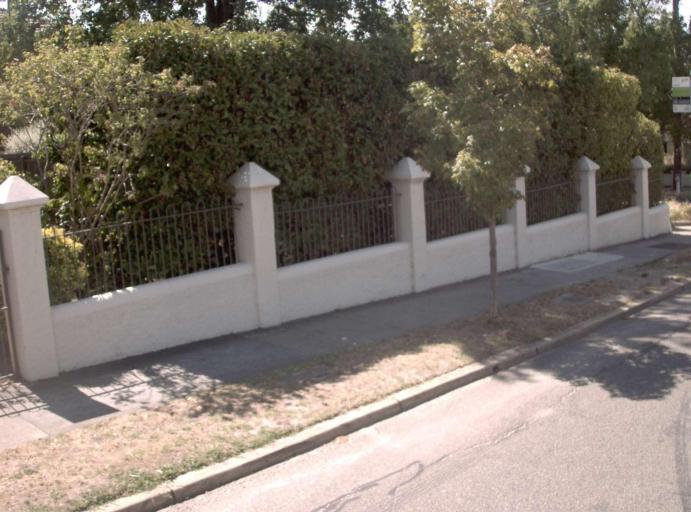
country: AU
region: Victoria
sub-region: Boroondara
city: Camberwell
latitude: -37.8392
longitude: 145.0658
